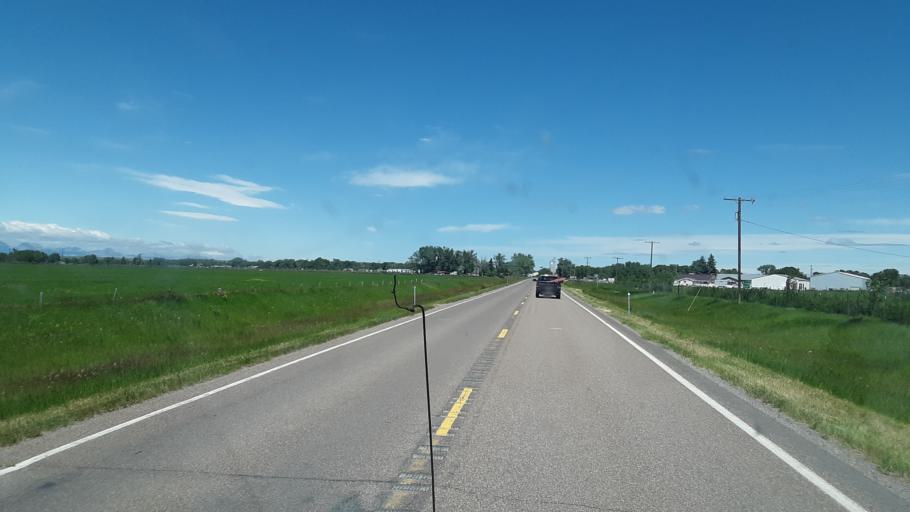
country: US
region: Montana
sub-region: Teton County
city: Choteau
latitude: 47.7955
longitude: -112.1685
